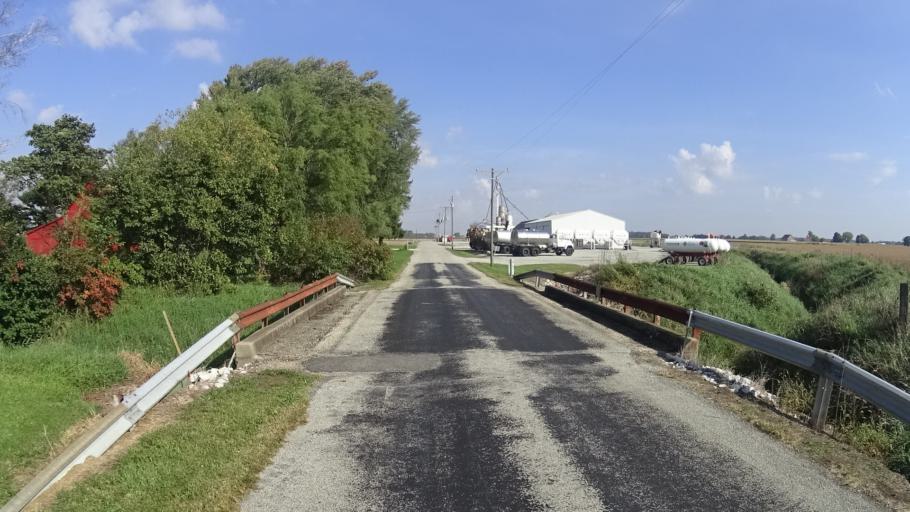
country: US
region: Indiana
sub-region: Madison County
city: Lapel
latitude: 40.0431
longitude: -85.8243
